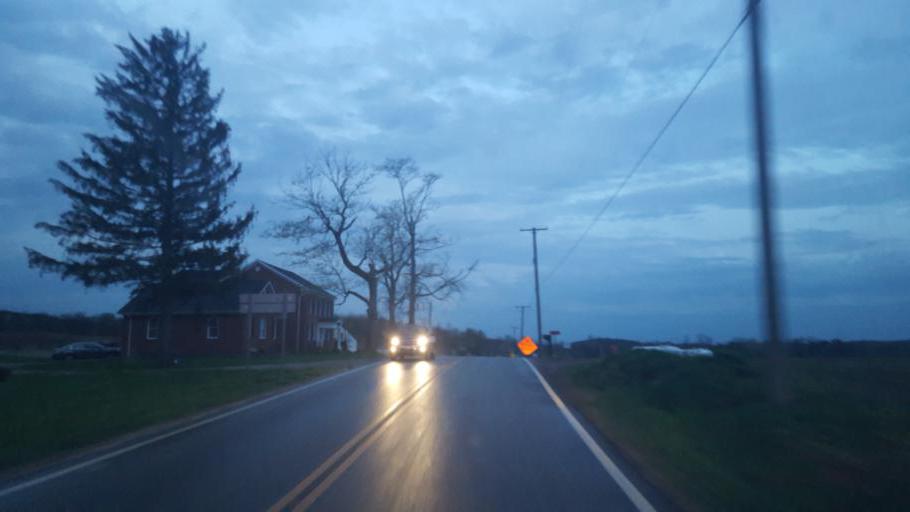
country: US
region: Ohio
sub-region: Ashland County
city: Ashland
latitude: 40.8213
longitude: -82.3928
